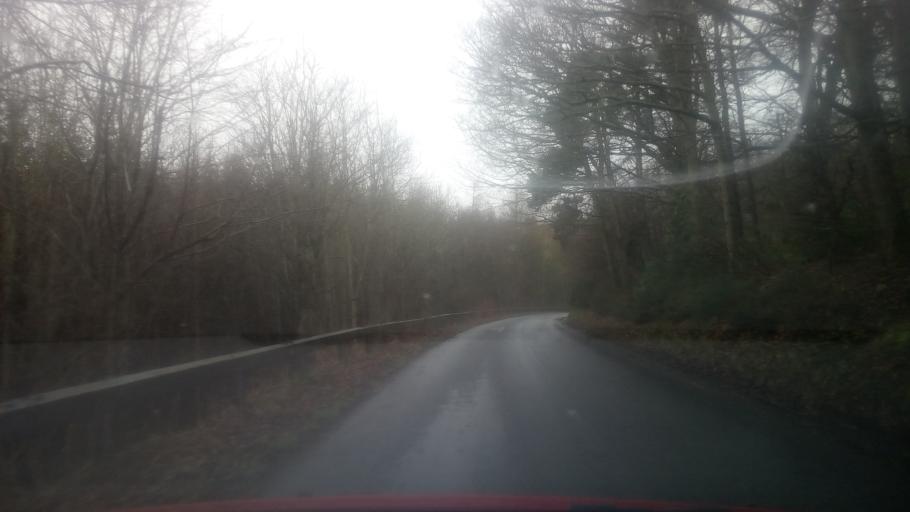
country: GB
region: Scotland
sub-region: The Scottish Borders
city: Earlston
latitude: 55.6292
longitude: -2.6768
